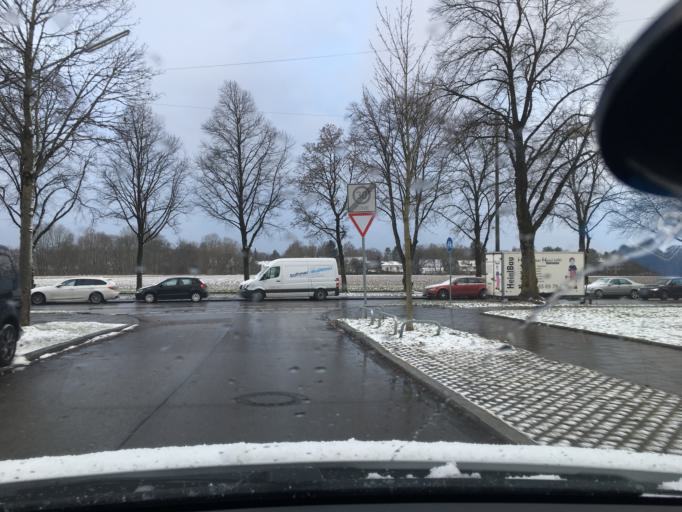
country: DE
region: Bavaria
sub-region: Upper Bavaria
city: Pullach im Isartal
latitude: 48.0908
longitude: 11.5349
